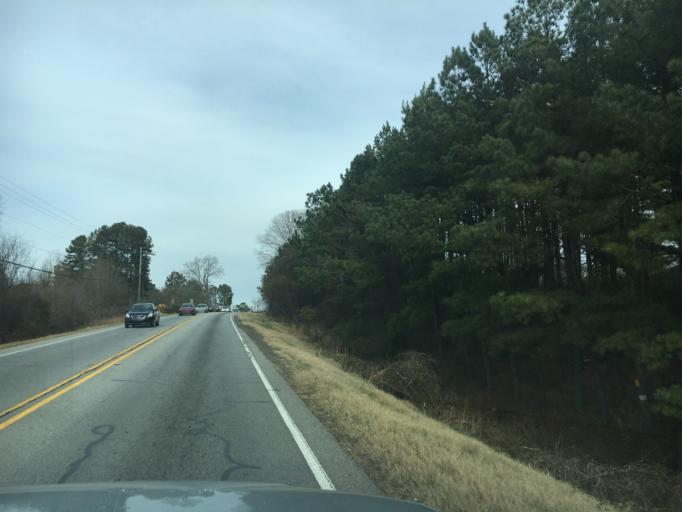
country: US
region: Georgia
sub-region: Barrow County
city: Winder
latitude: 33.9821
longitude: -83.7359
